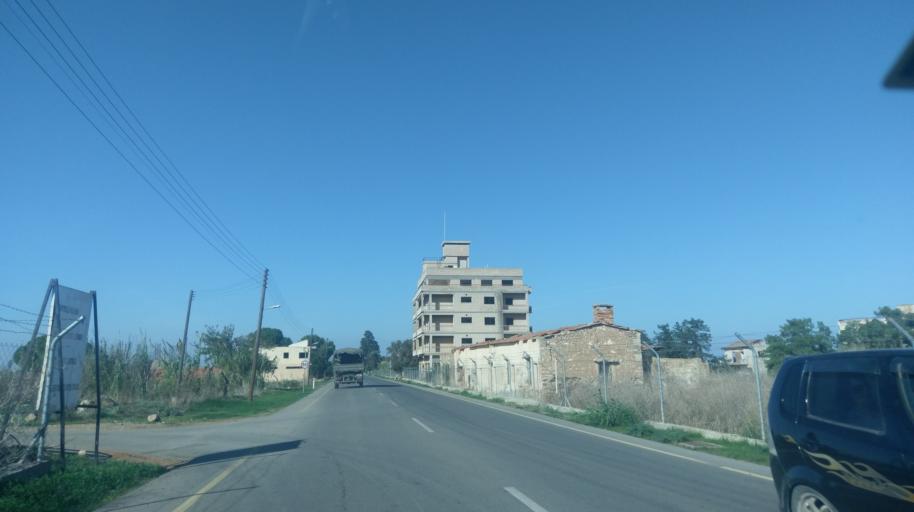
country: CY
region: Ammochostos
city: Deryneia
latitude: 35.0849
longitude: 33.9555
